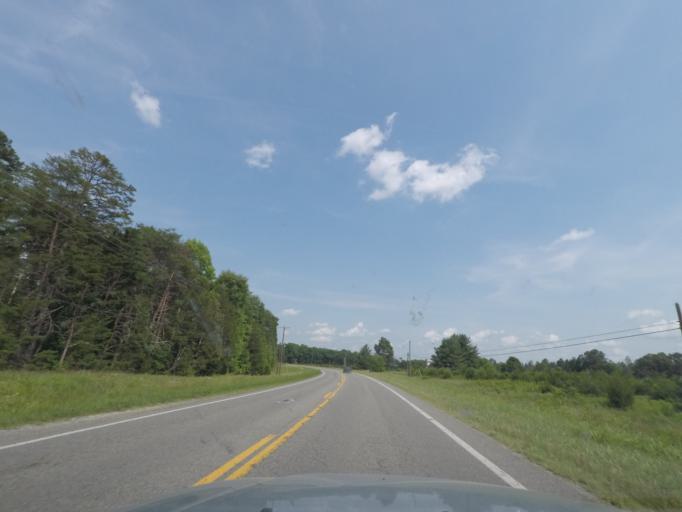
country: US
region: Virginia
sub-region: Fluvanna County
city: Palmyra
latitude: 37.8168
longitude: -78.2598
